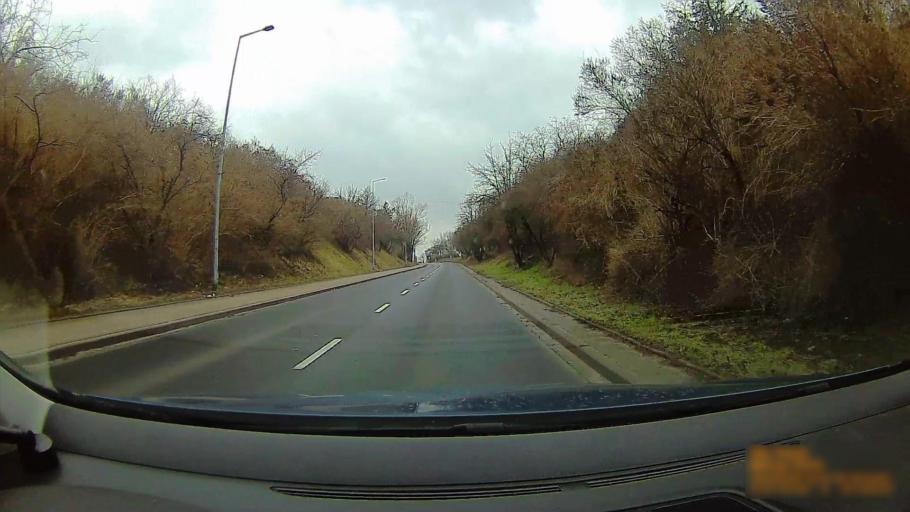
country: PL
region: Greater Poland Voivodeship
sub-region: Konin
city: Konin
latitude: 52.2016
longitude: 18.2616
